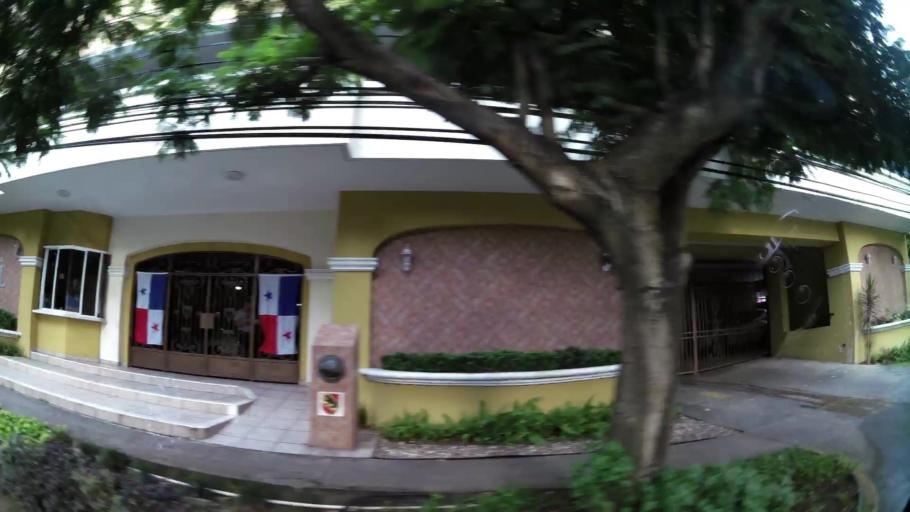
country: PA
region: Panama
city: Panama
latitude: 8.9906
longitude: -79.5050
